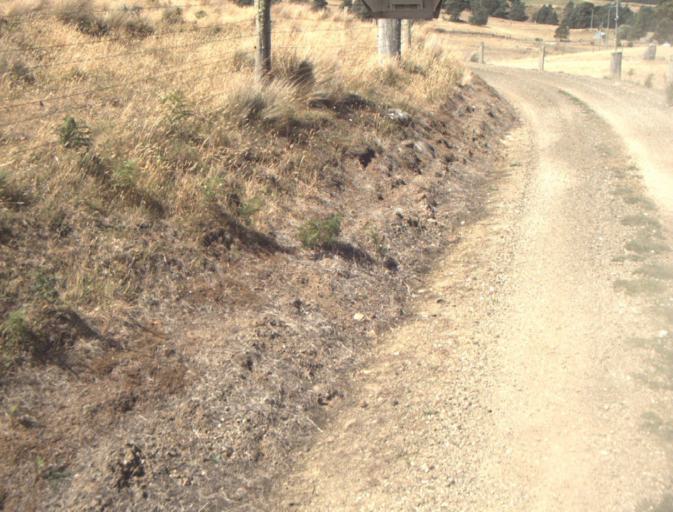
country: AU
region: Tasmania
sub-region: Dorset
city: Scottsdale
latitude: -41.3515
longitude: 147.4466
